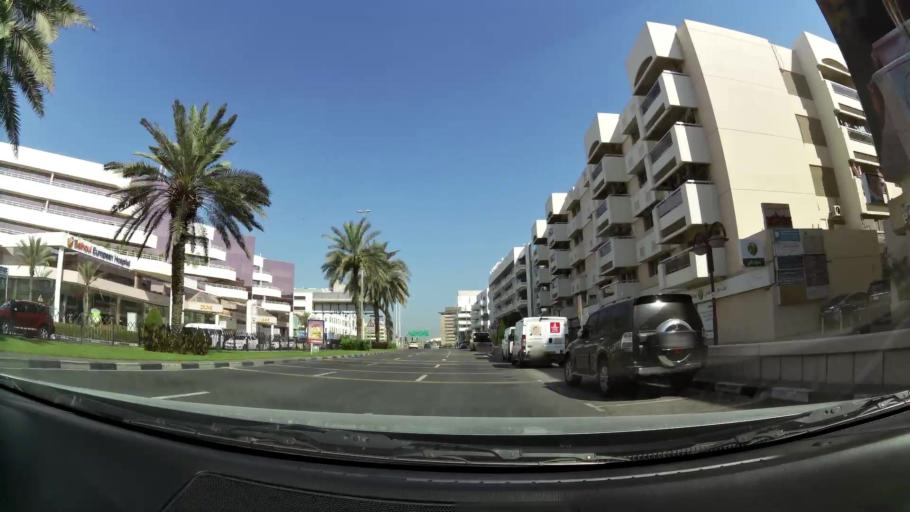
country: AE
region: Ash Shariqah
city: Sharjah
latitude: 25.2370
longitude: 55.2761
